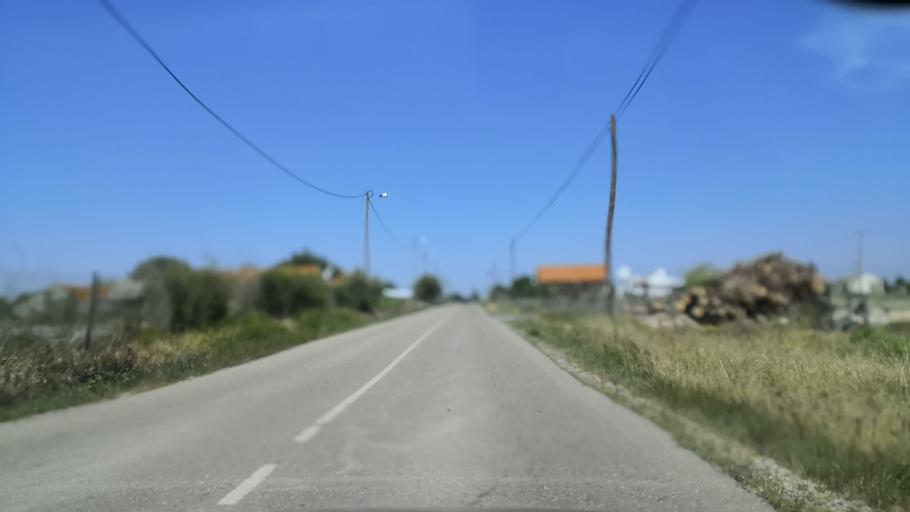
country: PT
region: Santarem
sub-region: Benavente
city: Poceirao
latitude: 38.6695
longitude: -8.7361
